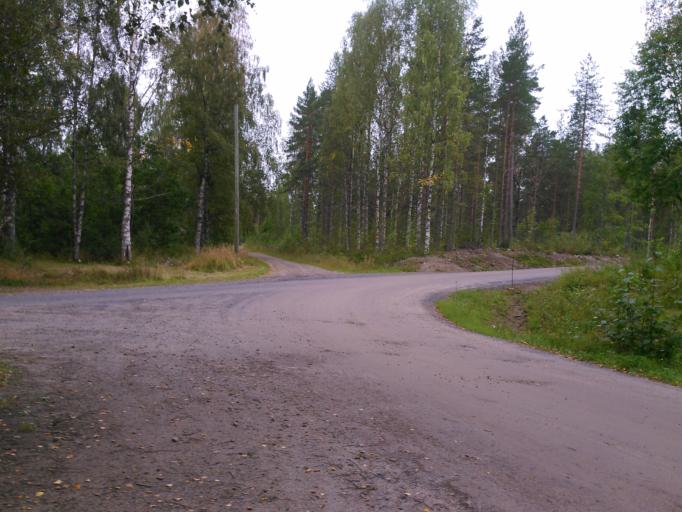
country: SE
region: Vaesterbotten
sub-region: Umea Kommun
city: Ersmark
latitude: 63.9320
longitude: 20.3851
